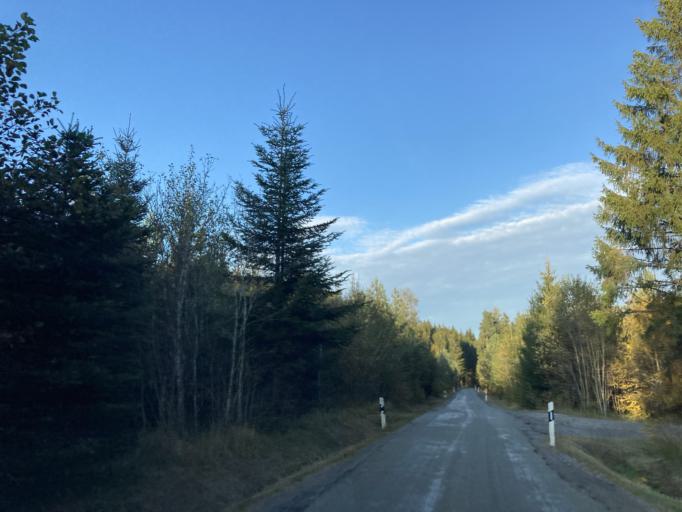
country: DE
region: Baden-Wuerttemberg
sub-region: Freiburg Region
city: Braunlingen
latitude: 47.9909
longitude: 8.3910
